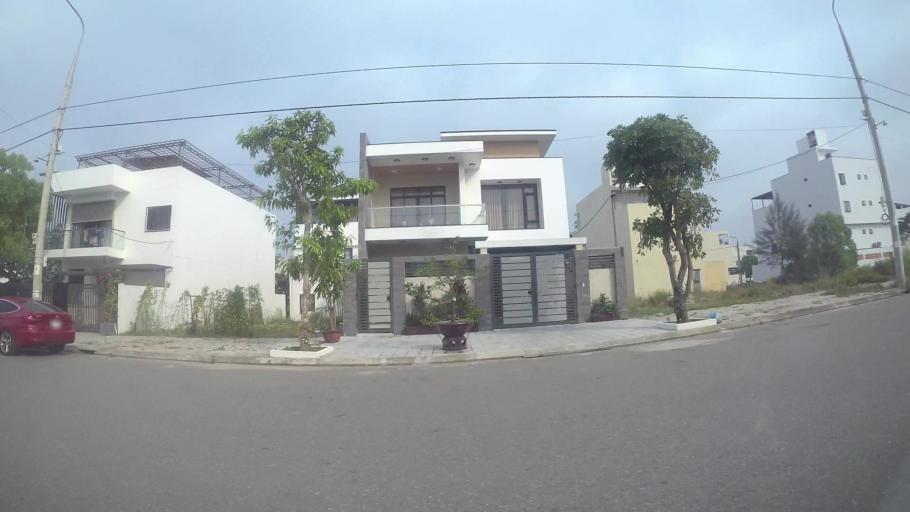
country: VN
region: Da Nang
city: Ngu Hanh Son
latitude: 16.0239
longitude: 108.2444
